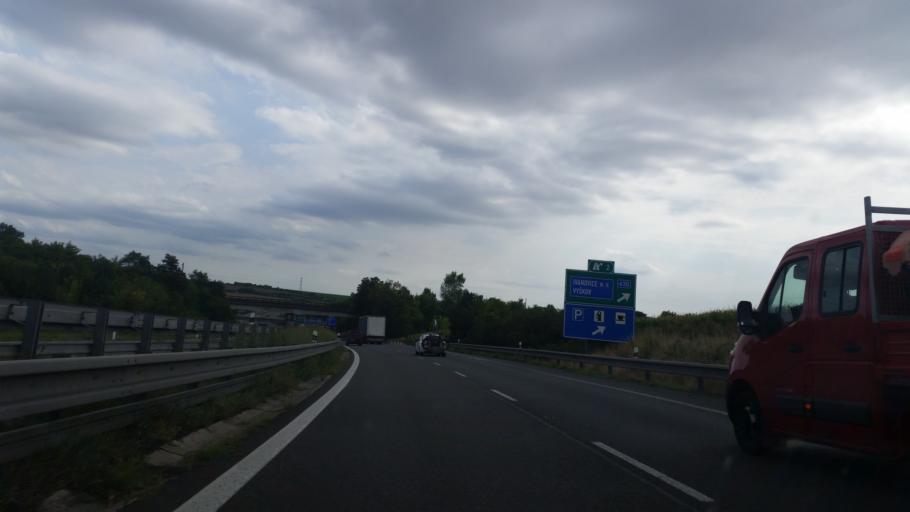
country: CZ
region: South Moravian
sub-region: Okres Vyskov
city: Vyskov
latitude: 49.2859
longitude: 17.0194
